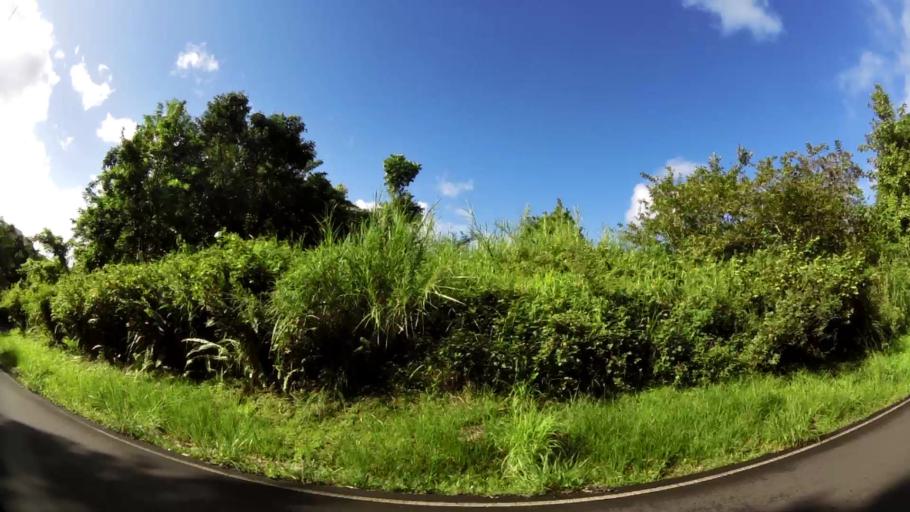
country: LC
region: Soufriere
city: Soufriere
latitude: 13.8688
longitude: -61.0460
